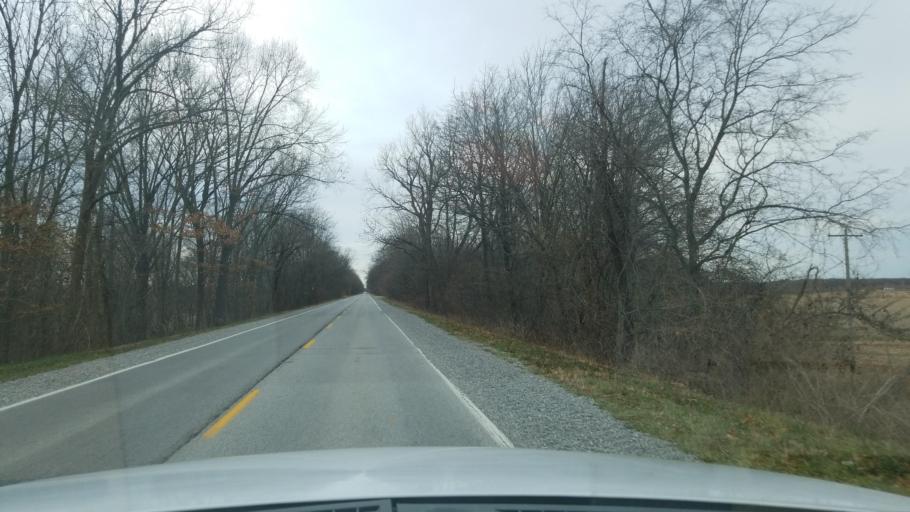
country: US
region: Illinois
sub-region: White County
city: Carmi
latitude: 37.9299
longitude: -88.0927
